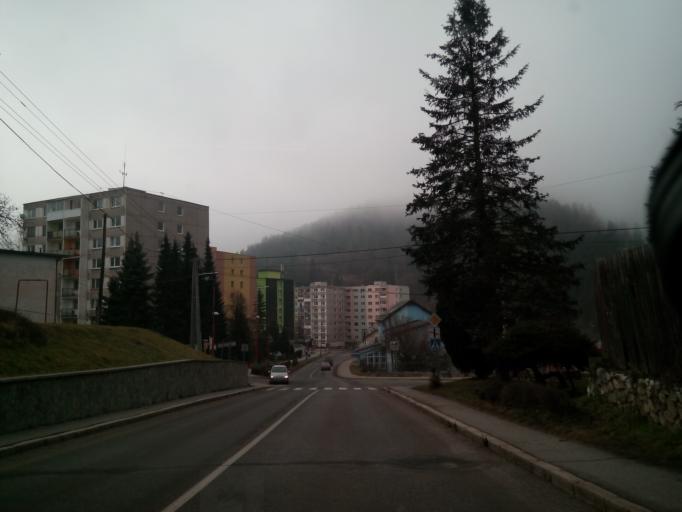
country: SK
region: Kosicky
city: Krompachy
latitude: 48.9170
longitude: 20.8754
